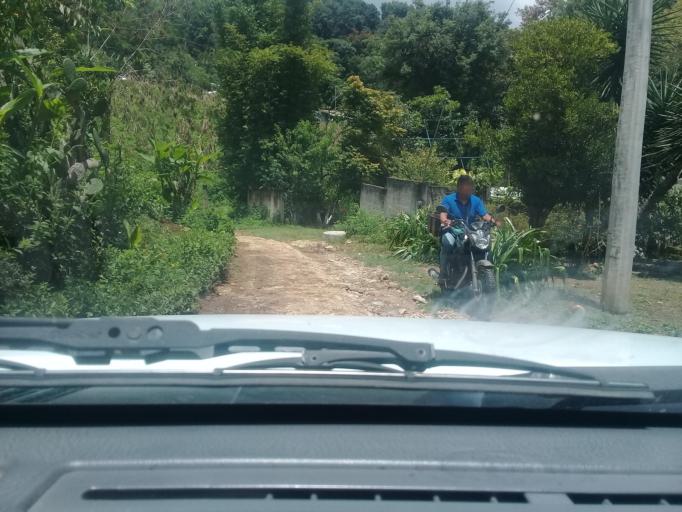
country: MX
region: Veracruz
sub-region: Tlalnelhuayocan
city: Otilpan
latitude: 19.5426
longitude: -96.9776
